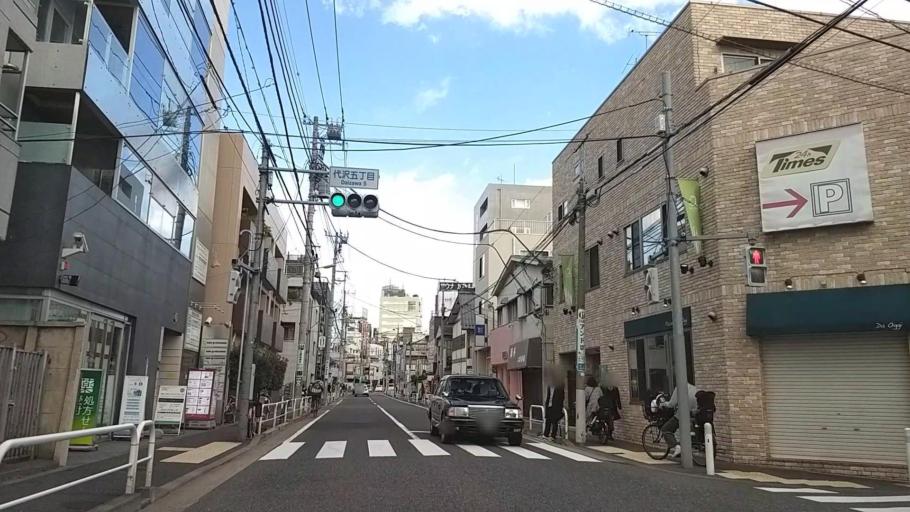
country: JP
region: Tokyo
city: Tokyo
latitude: 35.6589
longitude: 139.6685
